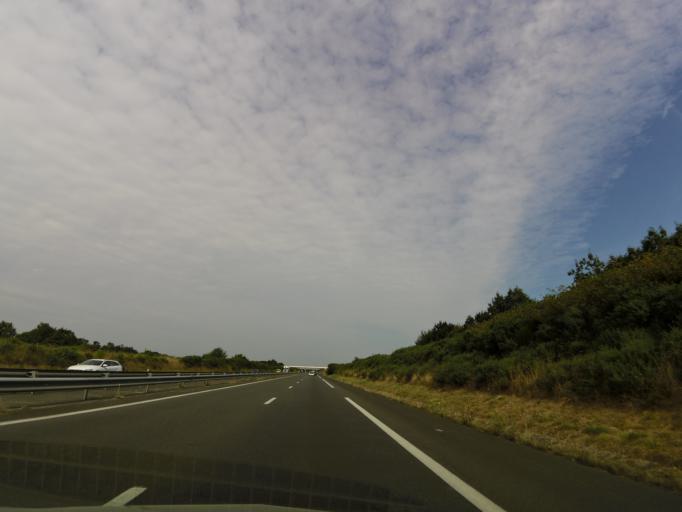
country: FR
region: Pays de la Loire
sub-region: Departement de la Loire-Atlantique
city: Le Bignon
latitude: 47.1014
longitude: -1.4749
